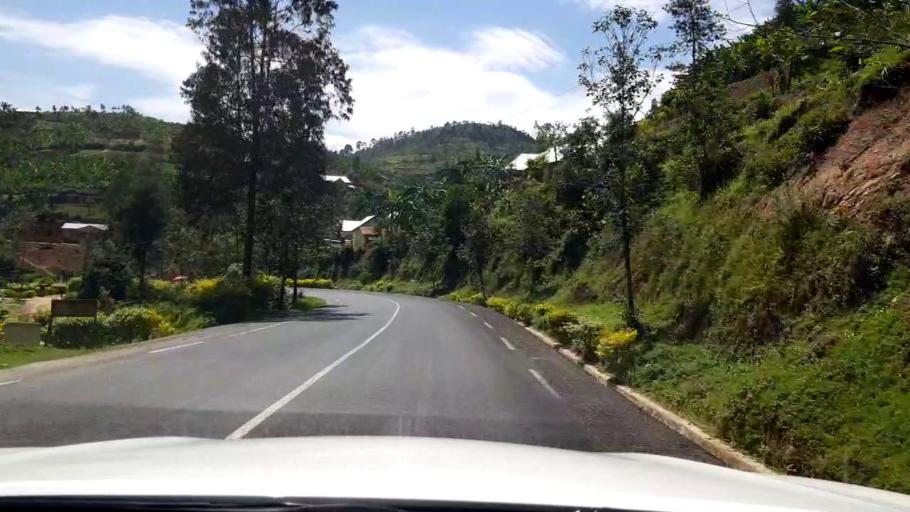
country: RW
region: Southern Province
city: Gitarama
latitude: -1.9192
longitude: 29.6385
